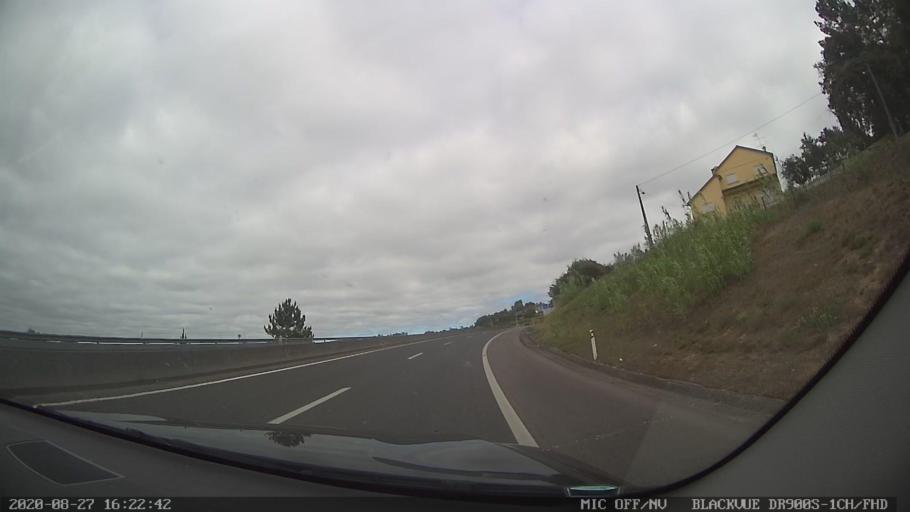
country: PT
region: Leiria
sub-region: Leiria
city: Leiria
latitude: 39.7483
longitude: -8.7800
